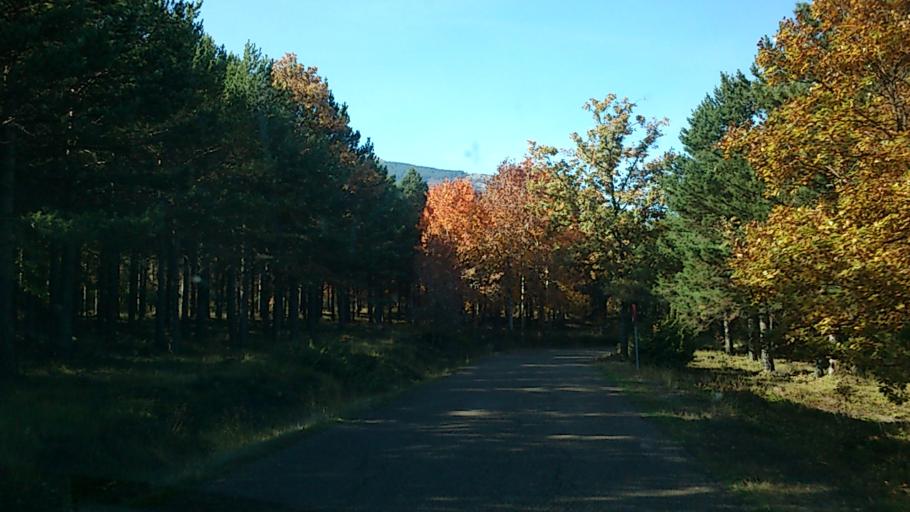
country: ES
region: Aragon
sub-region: Provincia de Zaragoza
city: Litago
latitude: 41.8045
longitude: -1.7903
